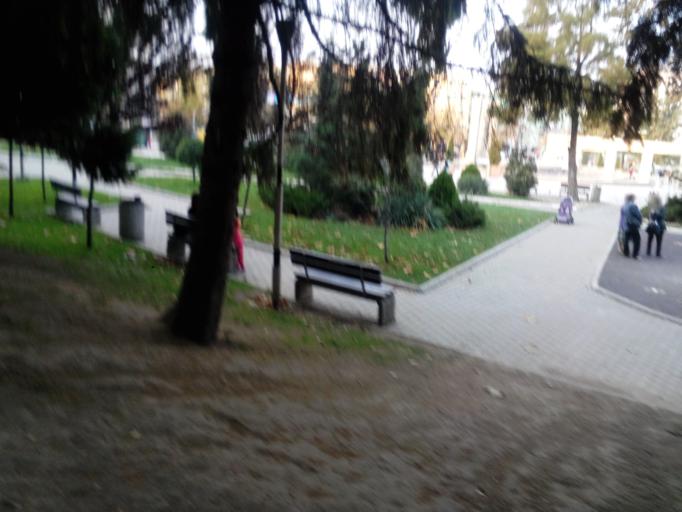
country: RO
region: Tulcea
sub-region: Municipiul Tulcea
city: Tulcea
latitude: 45.1768
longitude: 28.8035
